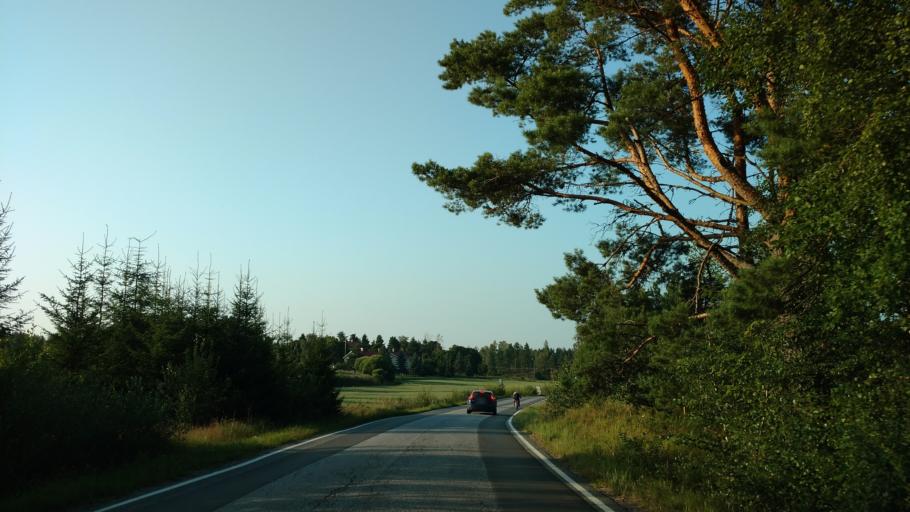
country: FI
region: Varsinais-Suomi
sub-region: Aboland-Turunmaa
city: Dragsfjaerd
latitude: 60.0701
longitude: 22.4508
